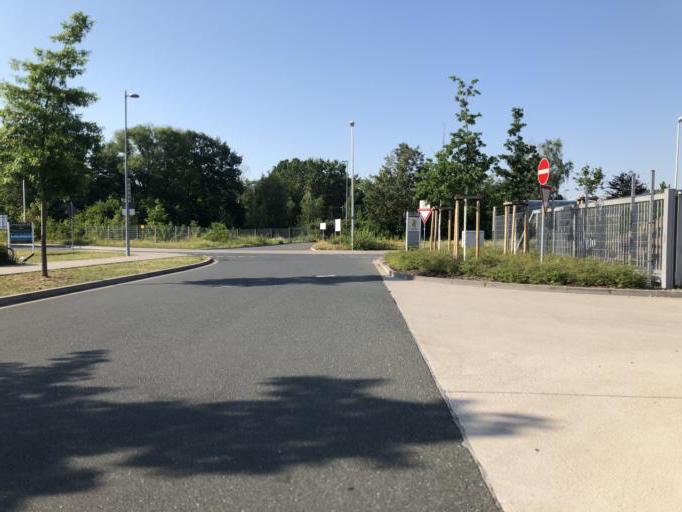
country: DE
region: Bavaria
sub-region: Regierungsbezirk Mittelfranken
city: Erlangen
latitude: 49.5641
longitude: 10.9733
